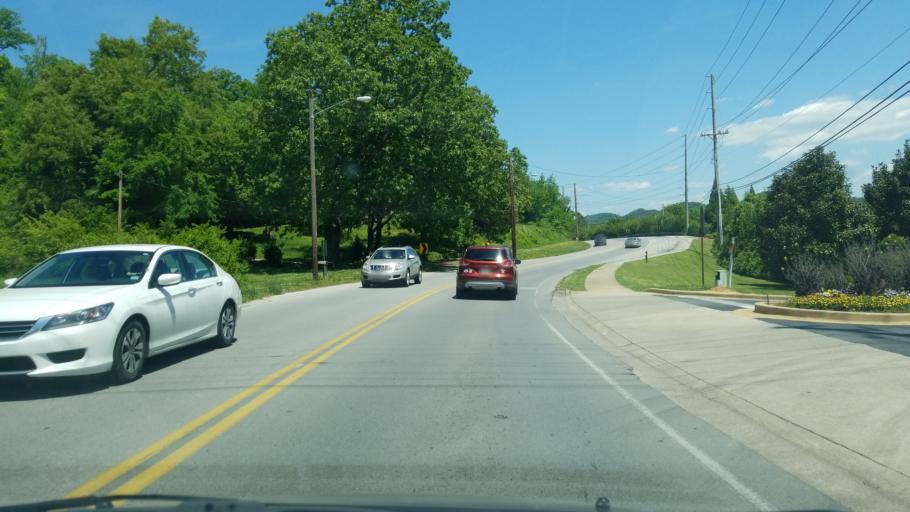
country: US
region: Tennessee
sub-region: Hamilton County
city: Red Bank
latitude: 35.1159
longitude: -85.3192
